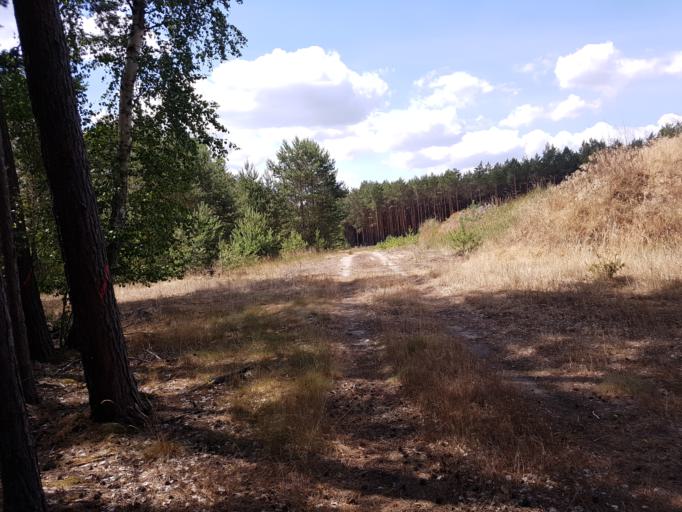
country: DE
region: Brandenburg
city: Heinersbruck
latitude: 51.7100
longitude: 14.4471
